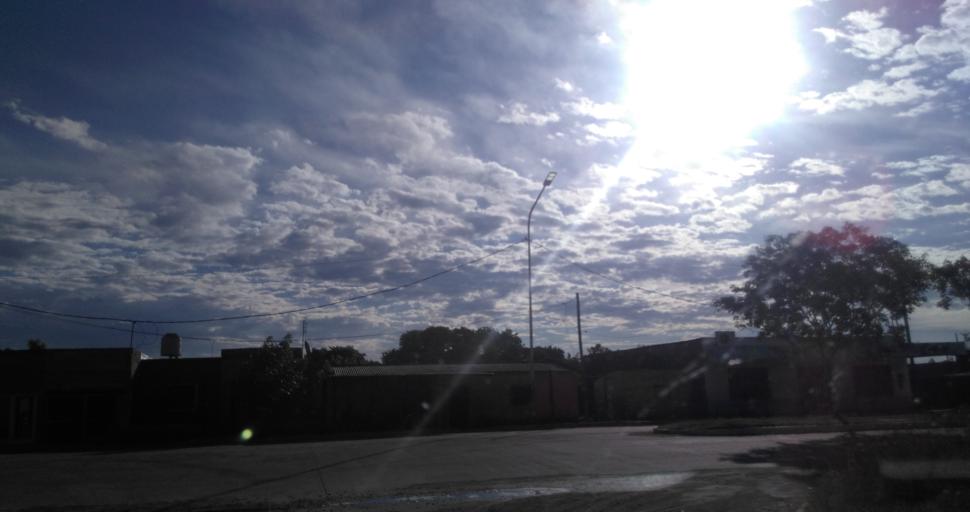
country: AR
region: Chaco
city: Fontana
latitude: -27.4126
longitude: -59.0296
